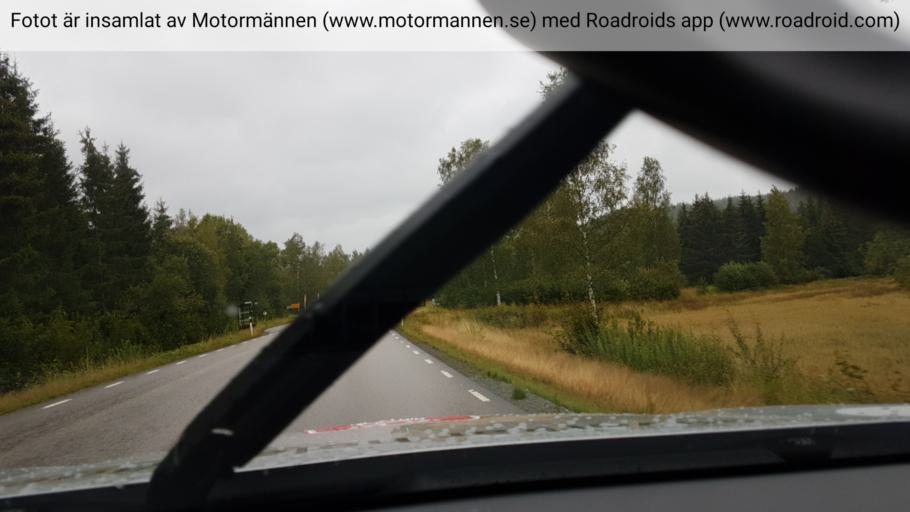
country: SE
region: Vaestra Goetaland
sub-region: Bengtsfors Kommun
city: Billingsfors
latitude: 58.9287
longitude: 12.2137
